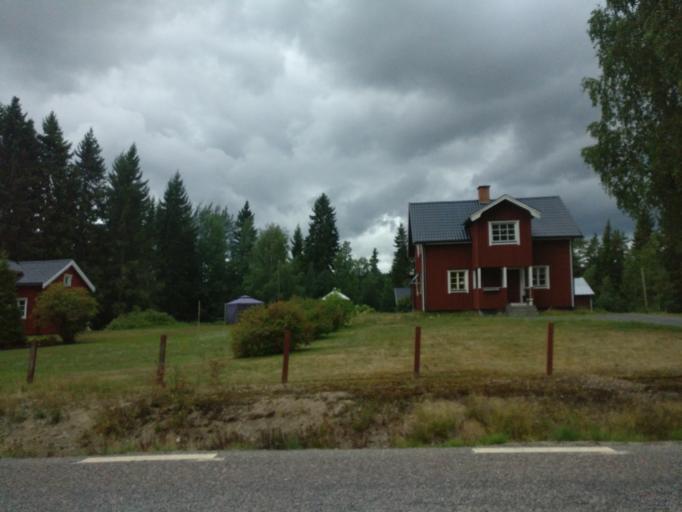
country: SE
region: Vaermland
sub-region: Torsby Kommun
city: Torsby
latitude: 60.7649
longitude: 12.7606
